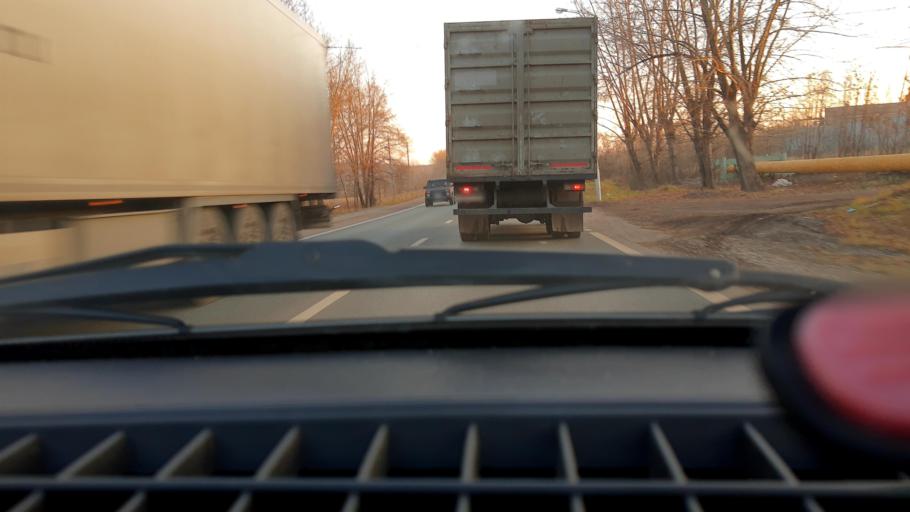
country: RU
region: Bashkortostan
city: Ufa
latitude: 54.8530
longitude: 56.1165
